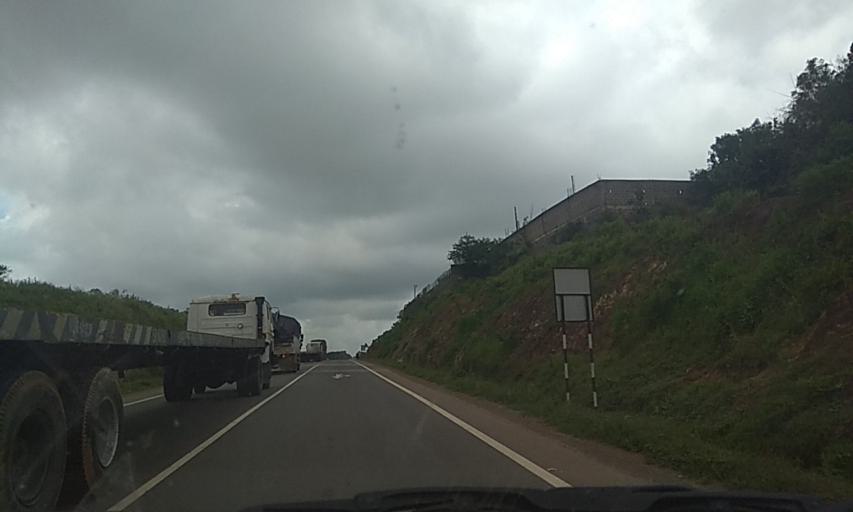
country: IN
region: Karnataka
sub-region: Dharwad
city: Hubli
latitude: 15.3606
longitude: 75.0501
